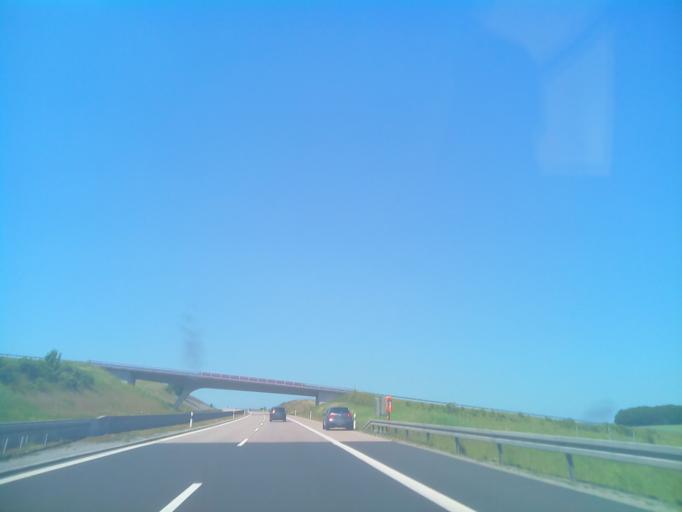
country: DE
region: Bavaria
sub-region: Regierungsbezirk Unterfranken
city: Hollstadt
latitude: 50.3548
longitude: 10.3171
